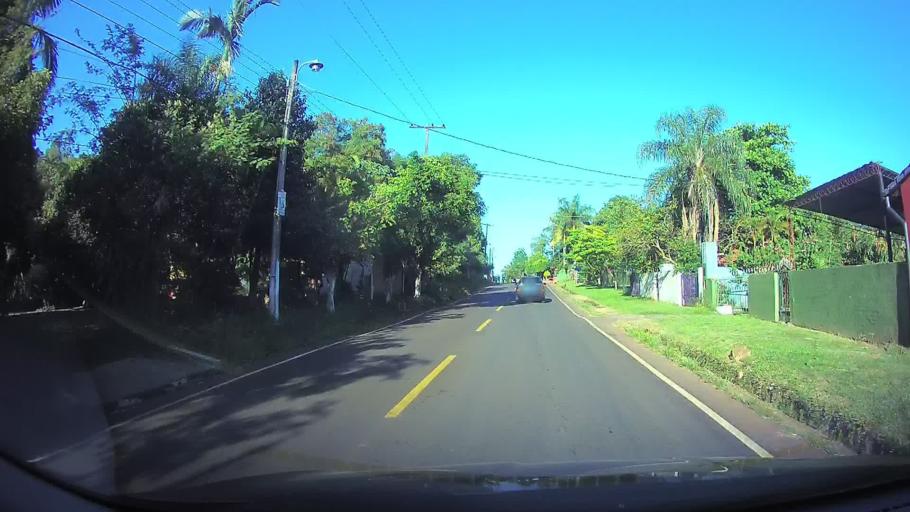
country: PY
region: Central
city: Limpio
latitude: -25.2478
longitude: -57.4932
